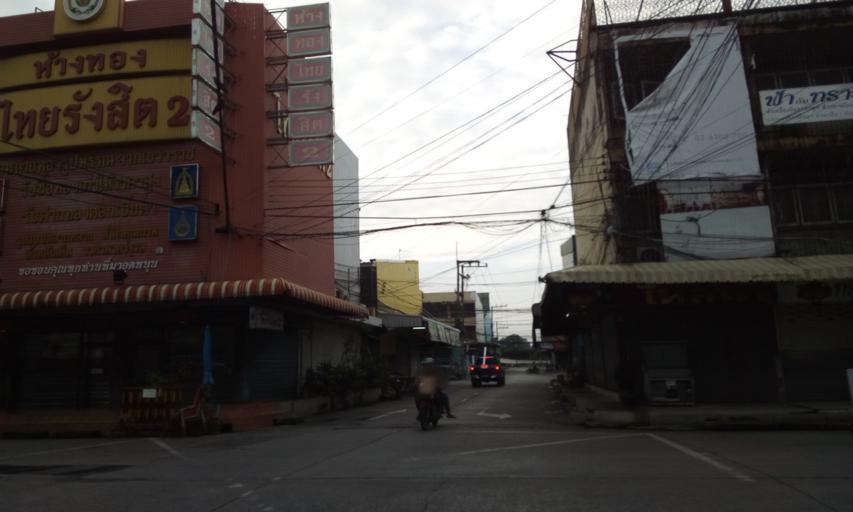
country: TH
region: Phra Nakhon Si Ayutthaya
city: Ban Bang Kadi Pathum Thani
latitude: 13.9852
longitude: 100.6148
